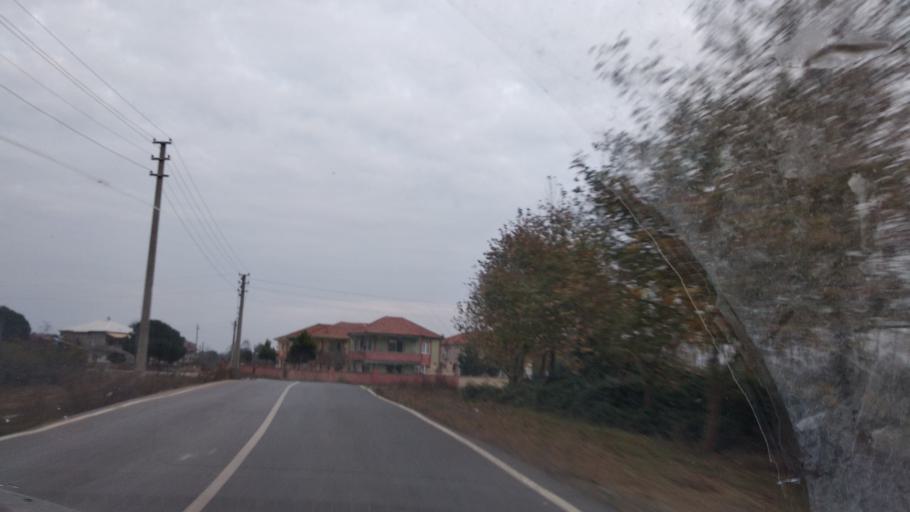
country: TR
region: Sakarya
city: Karasu
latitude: 41.0840
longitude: 30.7370
